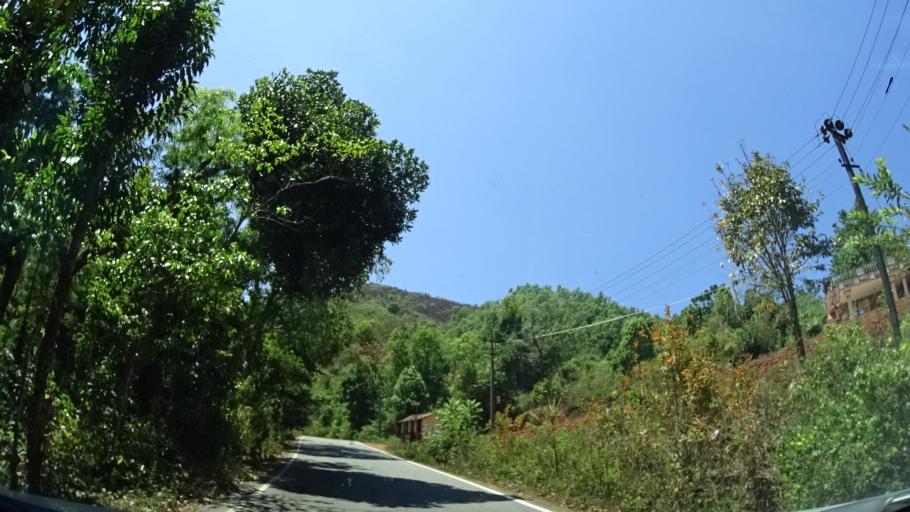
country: IN
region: Karnataka
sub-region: Chikmagalur
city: Sringeri
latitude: 13.2013
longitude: 75.2849
